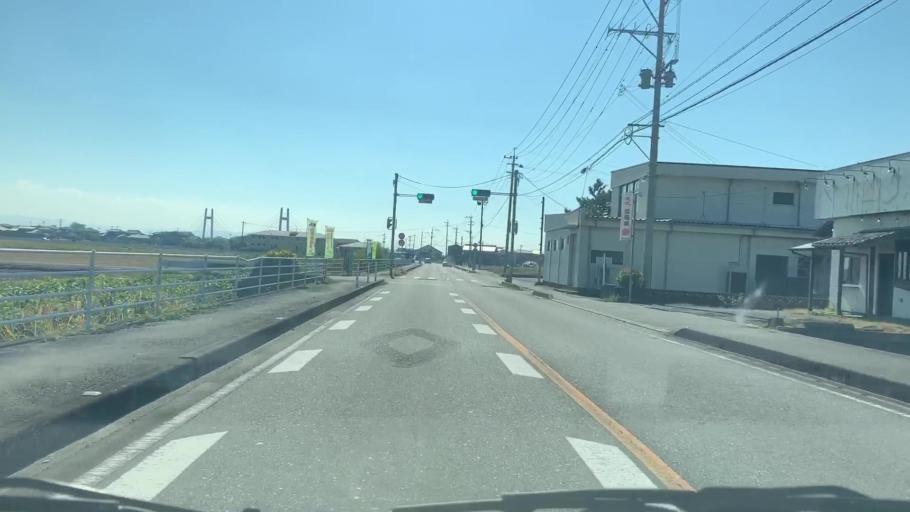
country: JP
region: Saga Prefecture
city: Kanzakimachi-kanzaki
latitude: 33.2928
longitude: 130.4454
